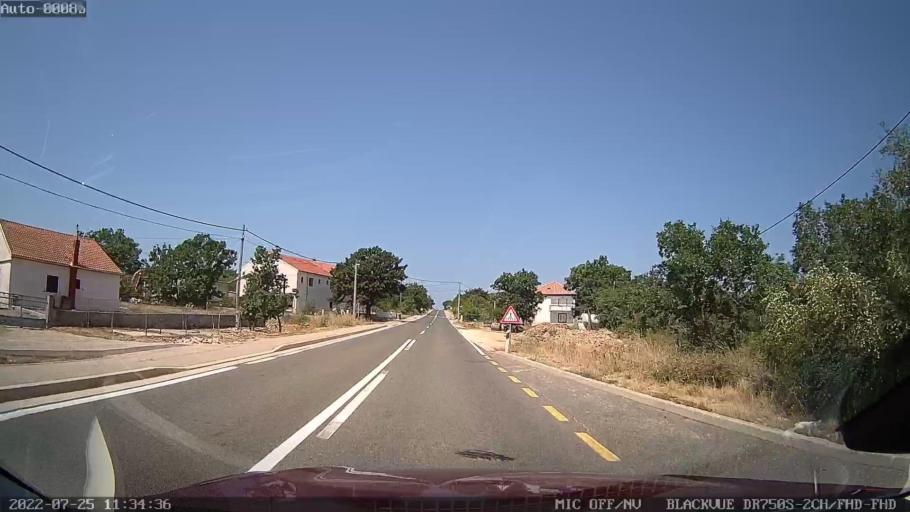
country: HR
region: Zadarska
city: Posedarje
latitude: 44.2304
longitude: 15.4199
